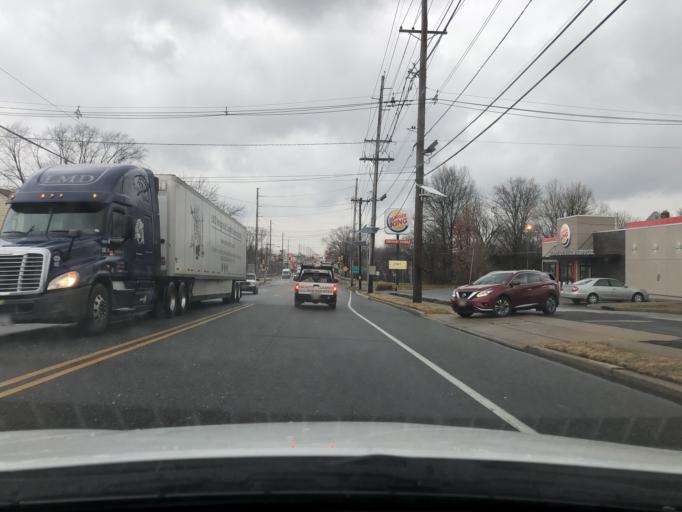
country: US
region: New Jersey
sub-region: Camden County
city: Bellmawr
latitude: 39.8708
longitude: -75.0814
